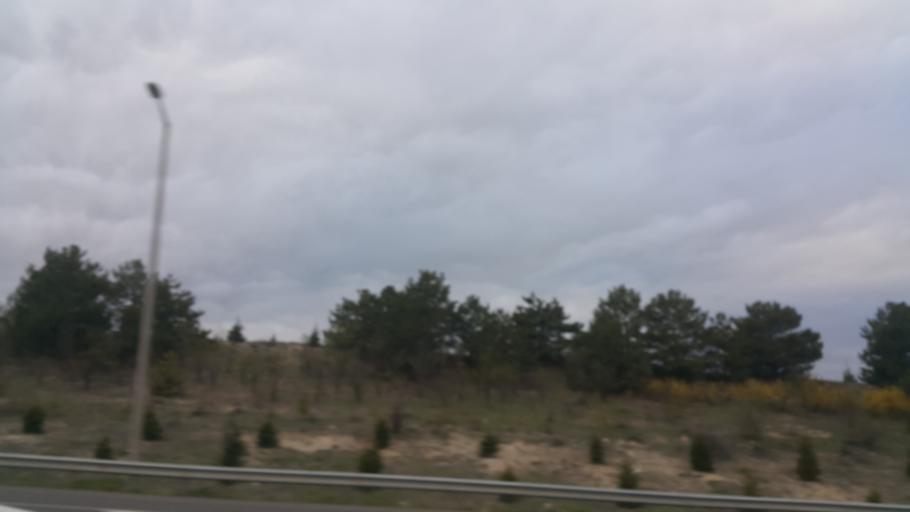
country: TR
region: Ankara
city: Etimesgut
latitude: 39.8555
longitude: 32.6257
